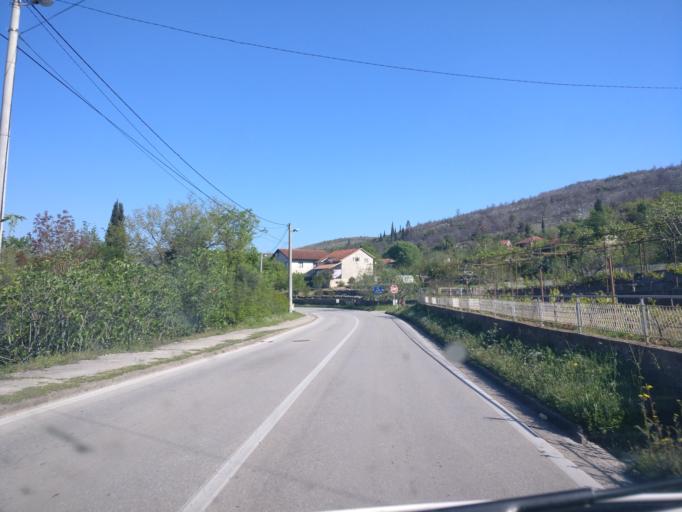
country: BA
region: Federation of Bosnia and Herzegovina
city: Capljina
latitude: 43.1250
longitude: 17.6816
